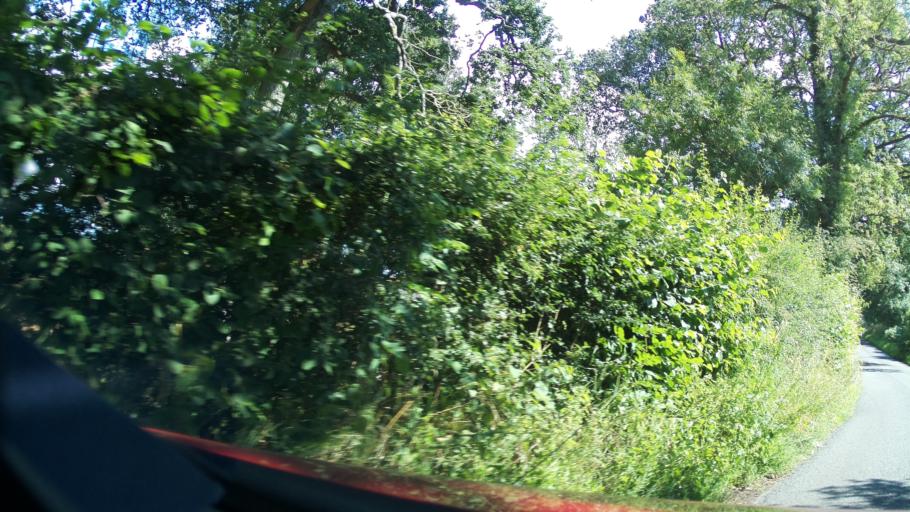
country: GB
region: England
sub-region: Hampshire
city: Kingsclere
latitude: 51.3477
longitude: -1.2829
